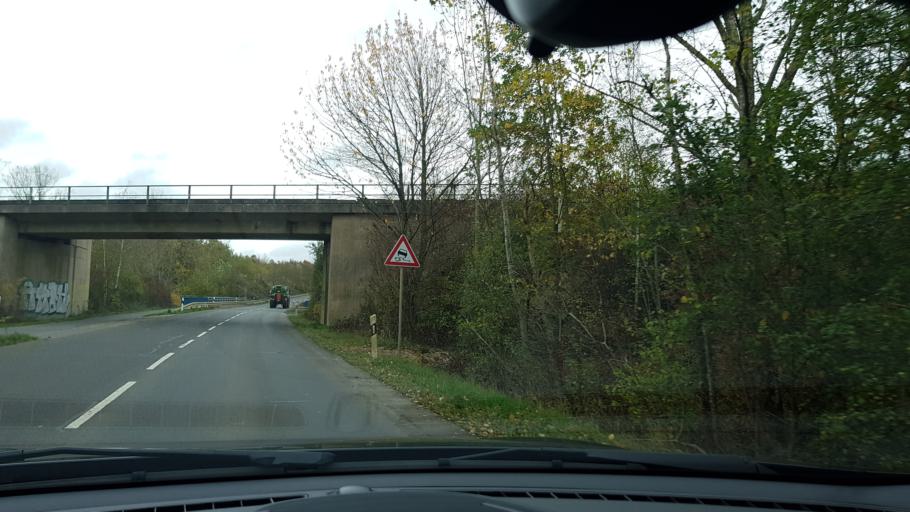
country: DE
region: North Rhine-Westphalia
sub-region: Regierungsbezirk Koln
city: Bedburg
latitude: 51.0392
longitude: 6.5664
